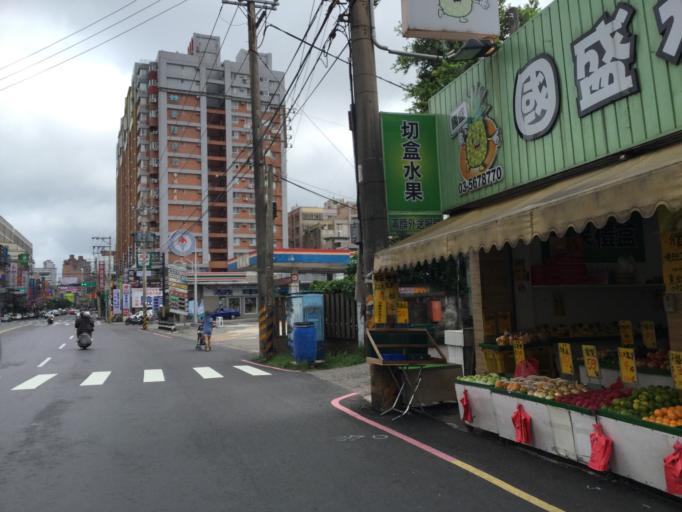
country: TW
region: Taiwan
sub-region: Hsinchu
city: Hsinchu
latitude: 24.7851
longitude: 121.0126
